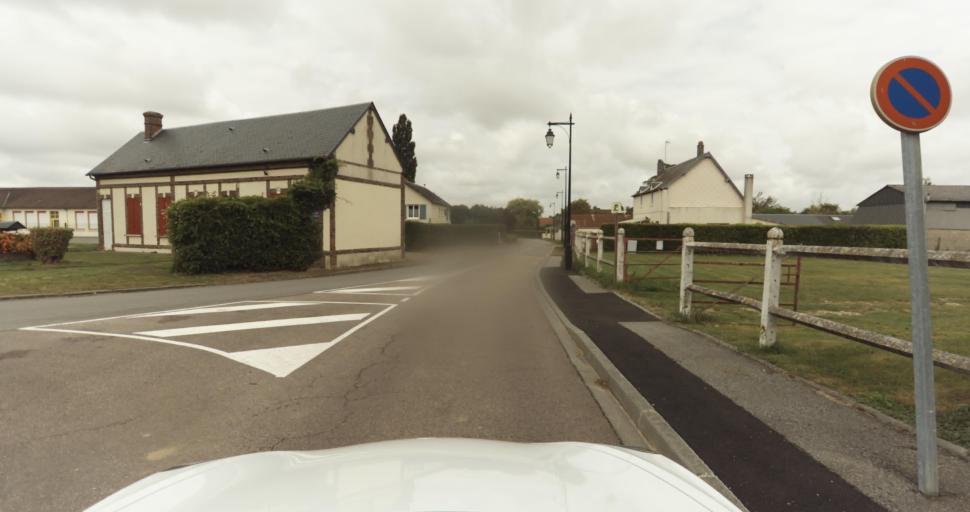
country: FR
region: Haute-Normandie
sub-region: Departement de l'Eure
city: Claville
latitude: 49.0248
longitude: 1.0349
